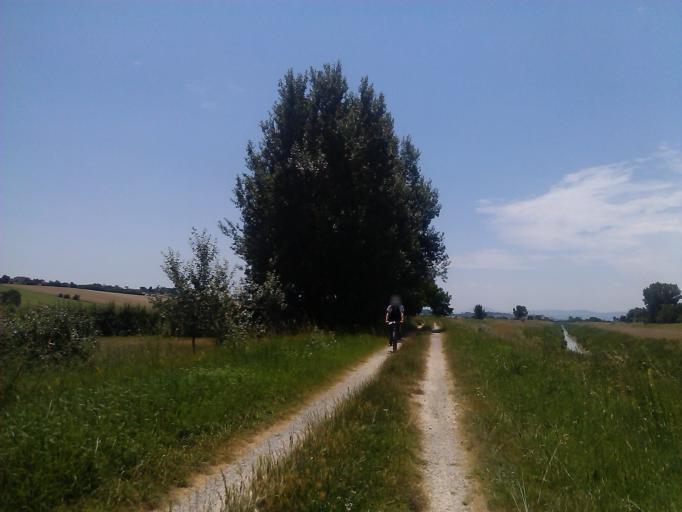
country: IT
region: Tuscany
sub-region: Province of Arezzo
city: Cesa
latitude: 43.2941
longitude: 11.8416
